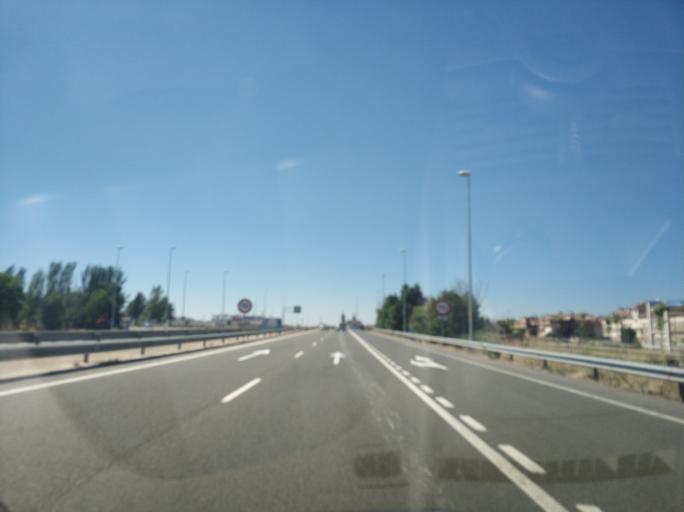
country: ES
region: Castille and Leon
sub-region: Provincia de Salamanca
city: Carbajosa de la Sagrada
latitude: 40.9465
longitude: -5.6456
